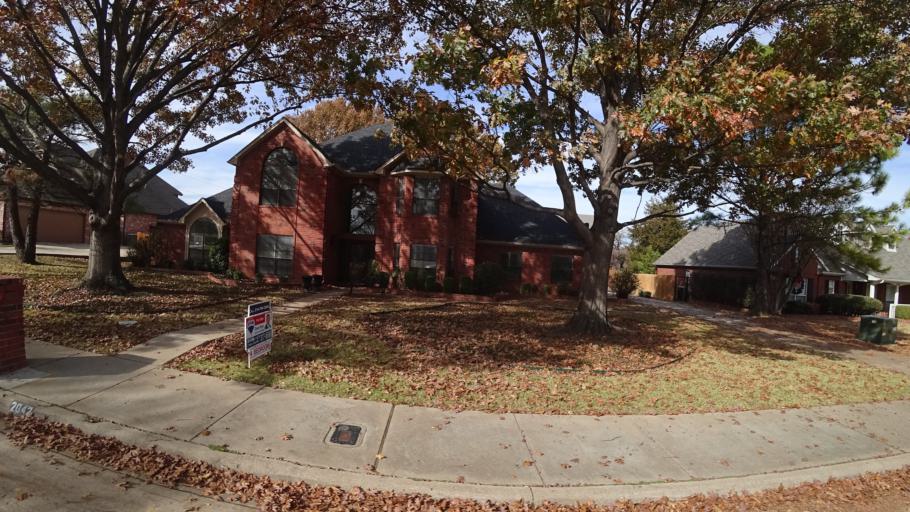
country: US
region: Texas
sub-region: Denton County
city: Highland Village
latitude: 33.0803
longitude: -97.0392
